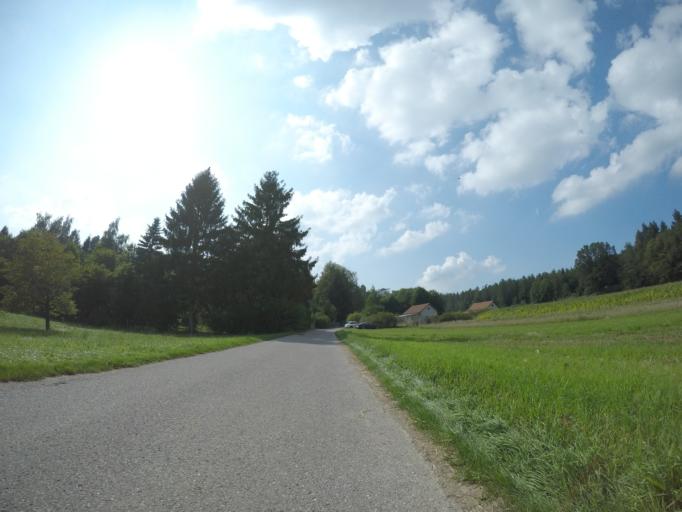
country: DE
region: Baden-Wuerttemberg
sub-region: Tuebingen Region
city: Reutlingen
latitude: 48.4587
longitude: 9.1915
